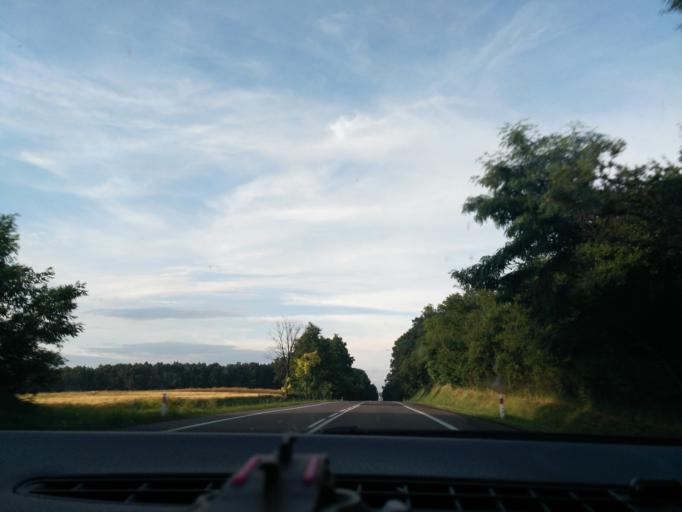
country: PL
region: Lublin Voivodeship
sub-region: Powiat krasnicki
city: Wilkolaz
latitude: 51.0304
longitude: 22.3682
